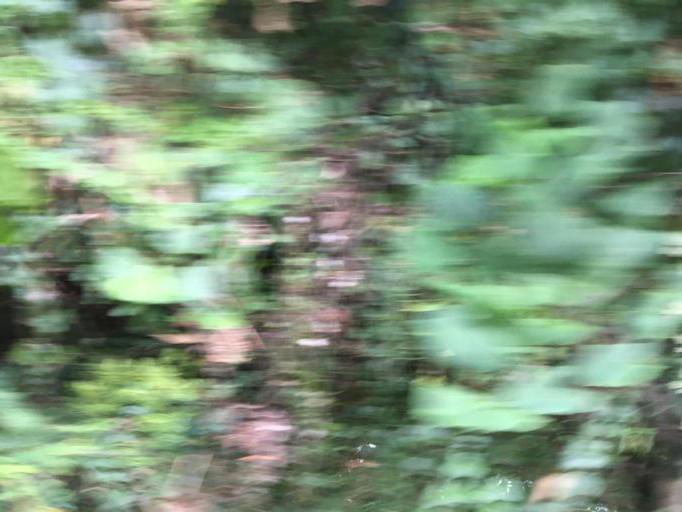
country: TW
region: Taiwan
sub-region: Chiayi
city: Jiayi Shi
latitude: 23.5379
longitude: 120.5613
